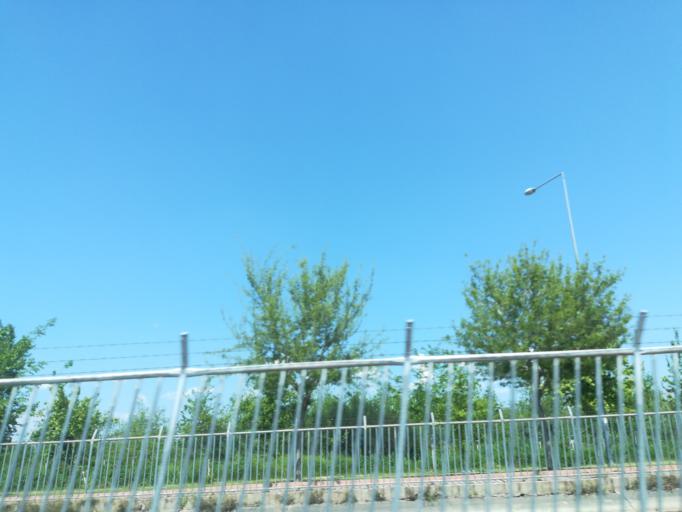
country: TR
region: Adana
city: Adana
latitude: 37.0227
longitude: 35.3700
